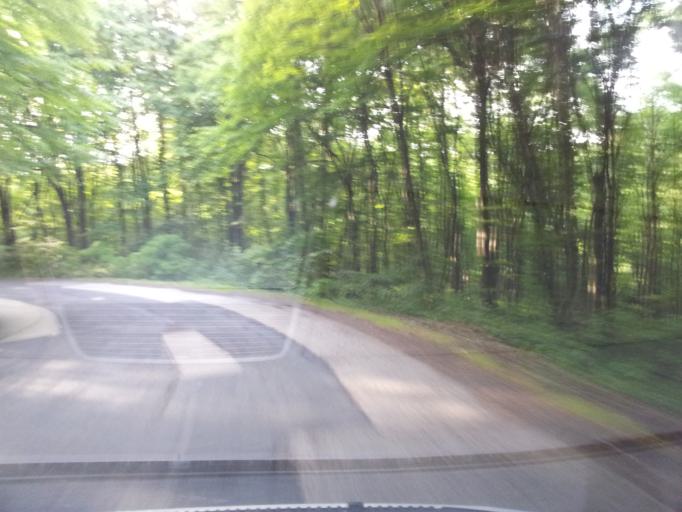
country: HU
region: Komarom-Esztergom
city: Kesztolc
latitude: 47.7360
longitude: 18.8160
